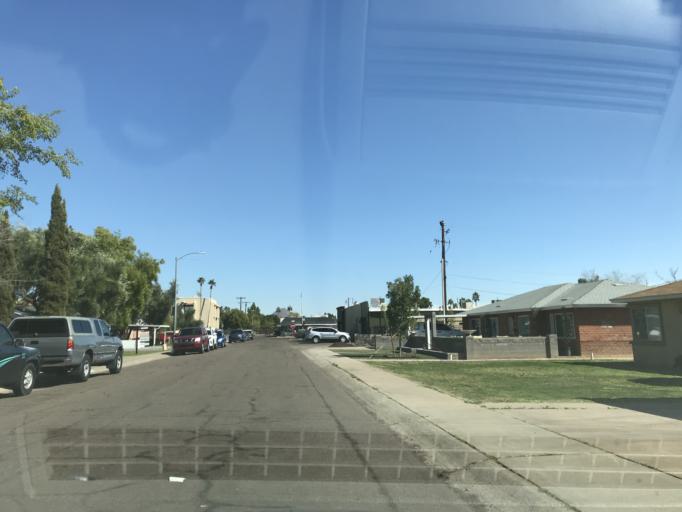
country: US
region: Arizona
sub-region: Maricopa County
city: Phoenix
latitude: 33.5175
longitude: -112.0839
